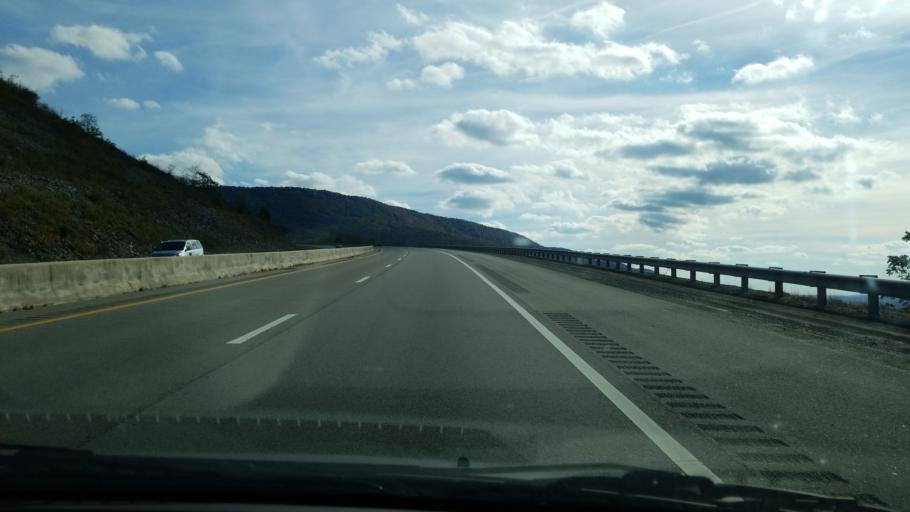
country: US
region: Tennessee
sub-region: Sequatchie County
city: Dunlap
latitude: 35.3738
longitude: -85.3323
